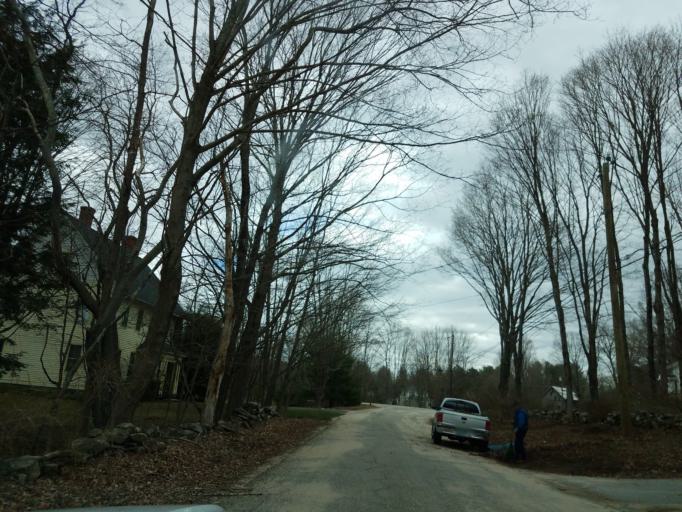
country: US
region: Connecticut
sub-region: Tolland County
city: Coventry Lake
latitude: 41.7601
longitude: -72.4015
